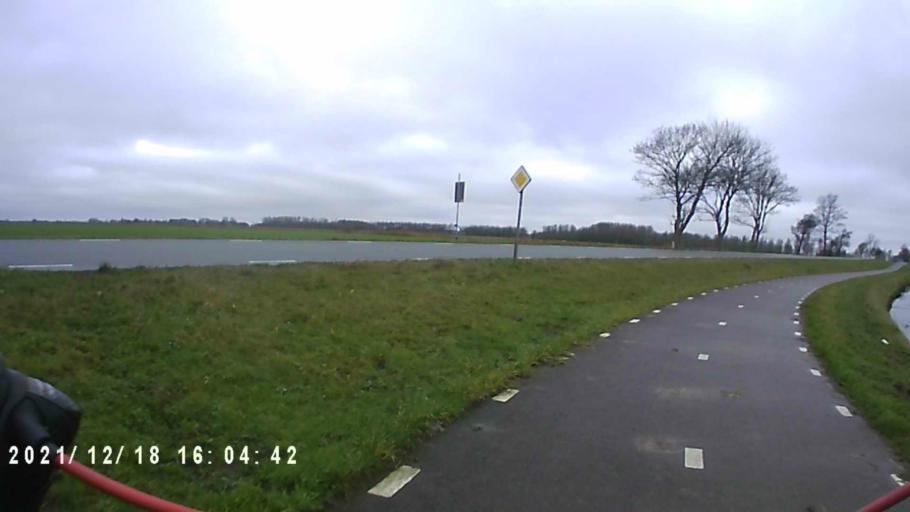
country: NL
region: Friesland
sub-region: Gemeente Dongeradeel
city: Anjum
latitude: 53.3523
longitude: 6.0774
